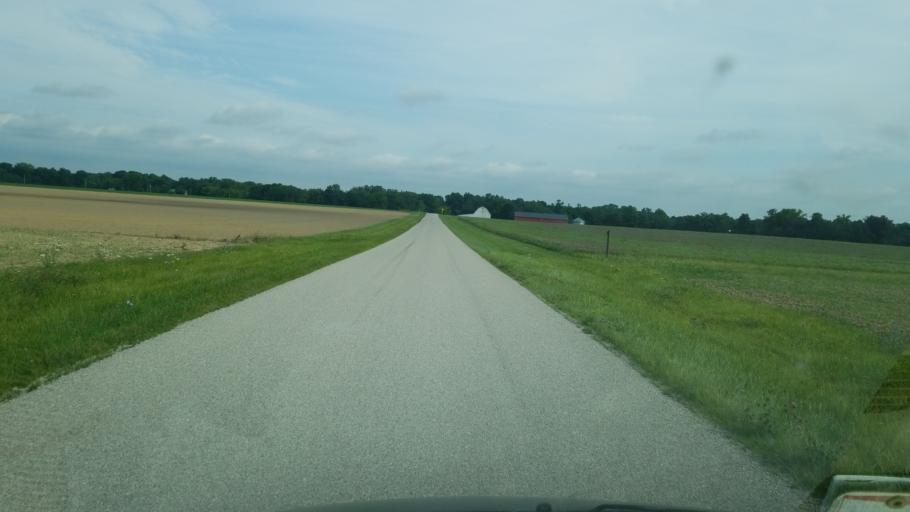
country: US
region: Ohio
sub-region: Seneca County
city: Tiffin
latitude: 41.1462
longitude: -83.0943
